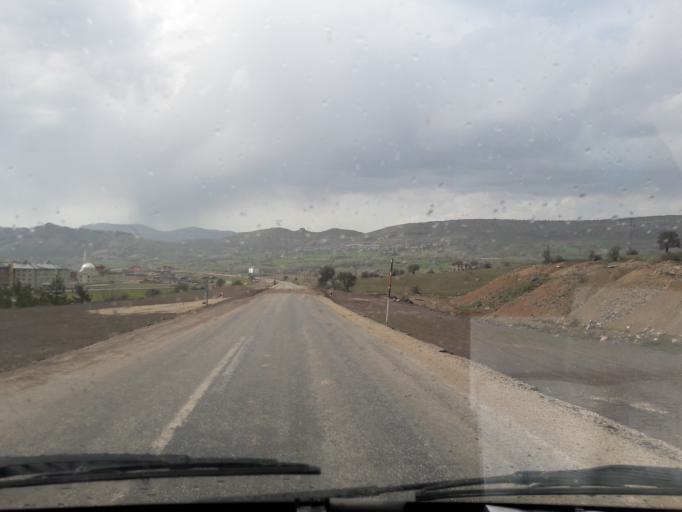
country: TR
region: Giresun
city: Alucra
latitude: 40.3216
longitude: 38.7733
